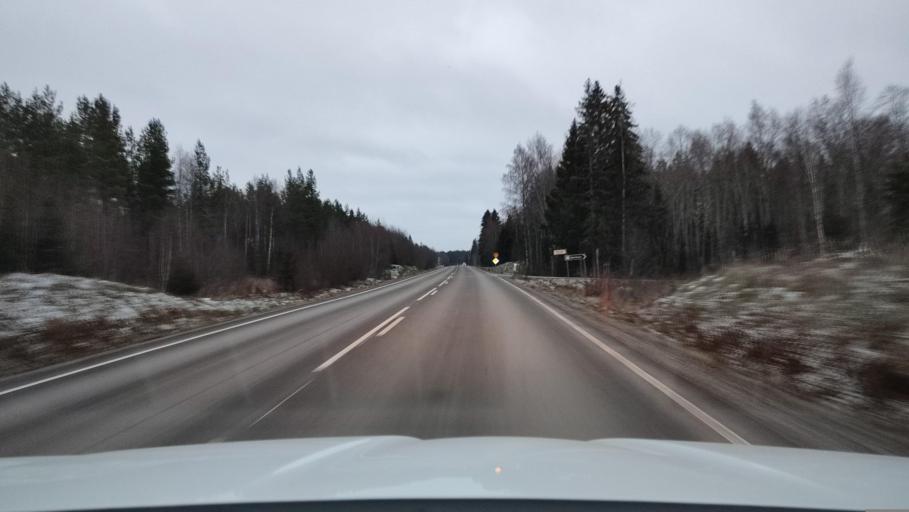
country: FI
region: Ostrobothnia
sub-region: Vaasa
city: Replot
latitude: 63.2168
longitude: 21.4258
